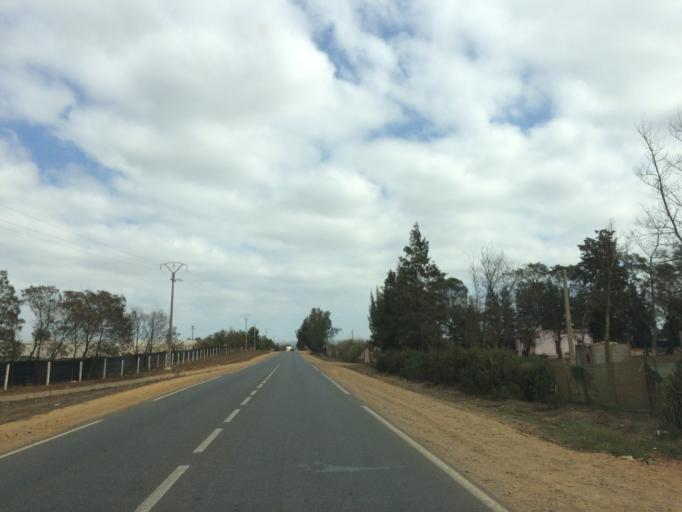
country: MA
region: Gharb-Chrarda-Beni Hssen
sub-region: Kenitra Province
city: Lalla Mimouna
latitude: 34.8418
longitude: -6.1705
